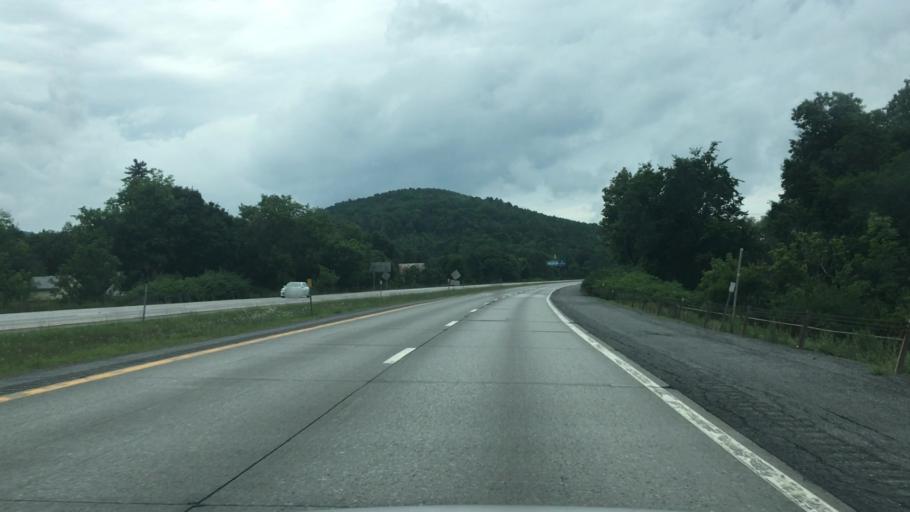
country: US
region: New York
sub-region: Schoharie County
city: Cobleskill
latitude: 42.6371
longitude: -74.5623
